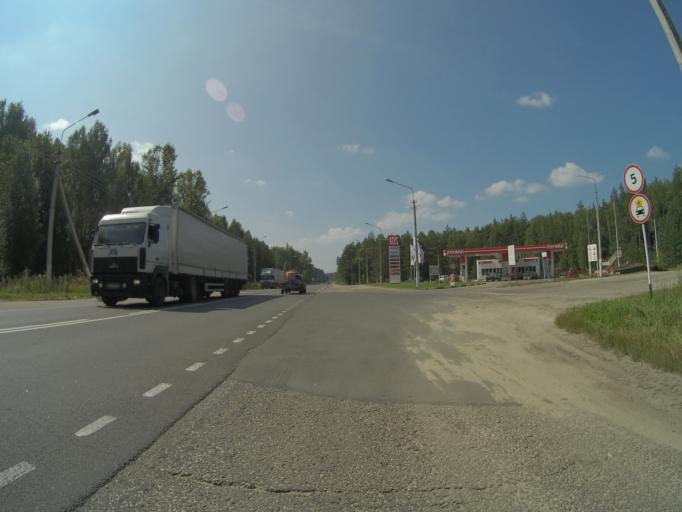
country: RU
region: Vladimir
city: Gus'-Khrustal'nyy
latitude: 55.6440
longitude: 40.7107
